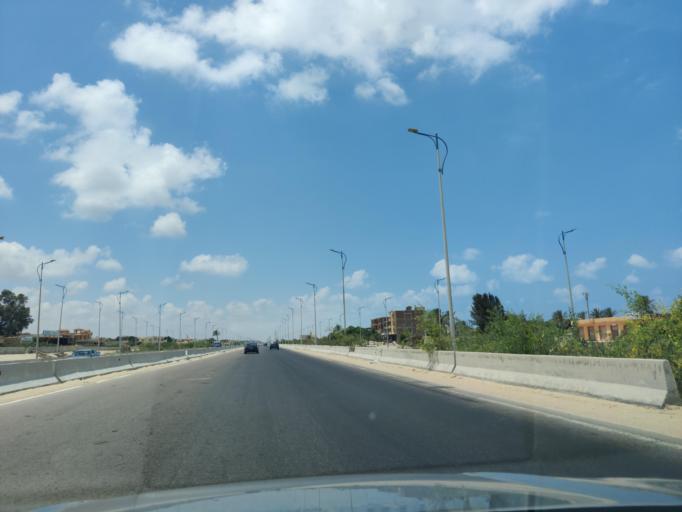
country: EG
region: Alexandria
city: Alexandria
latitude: 31.0009
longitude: 29.6118
